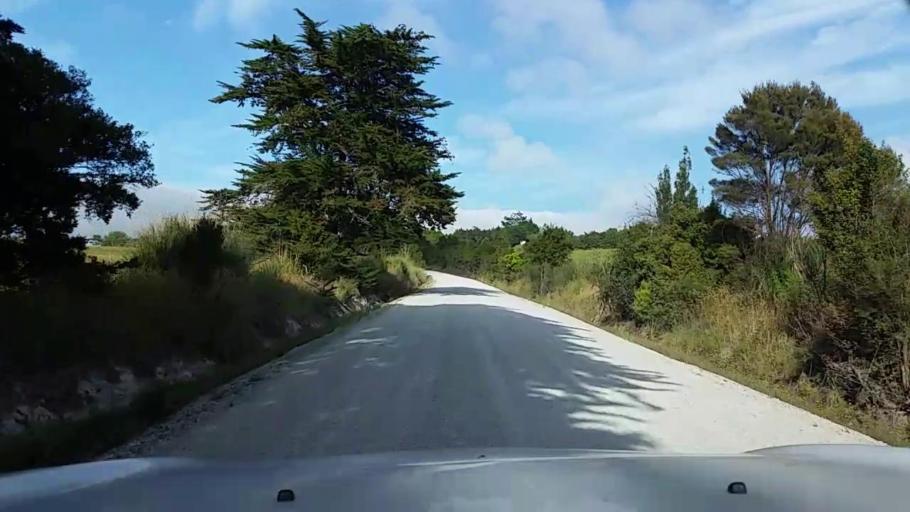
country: NZ
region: Northland
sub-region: Whangarei
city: Maungatapere
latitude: -35.6840
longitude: 174.1889
